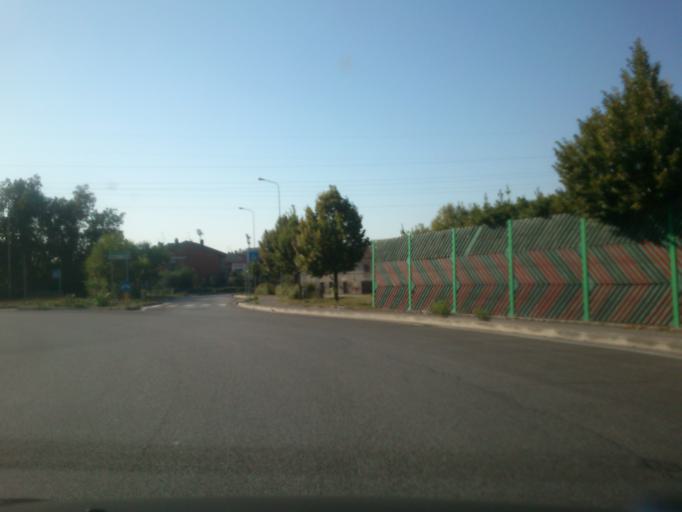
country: IT
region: The Marches
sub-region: Provincia di Pesaro e Urbino
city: Pesaro
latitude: 43.8895
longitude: 12.9004
